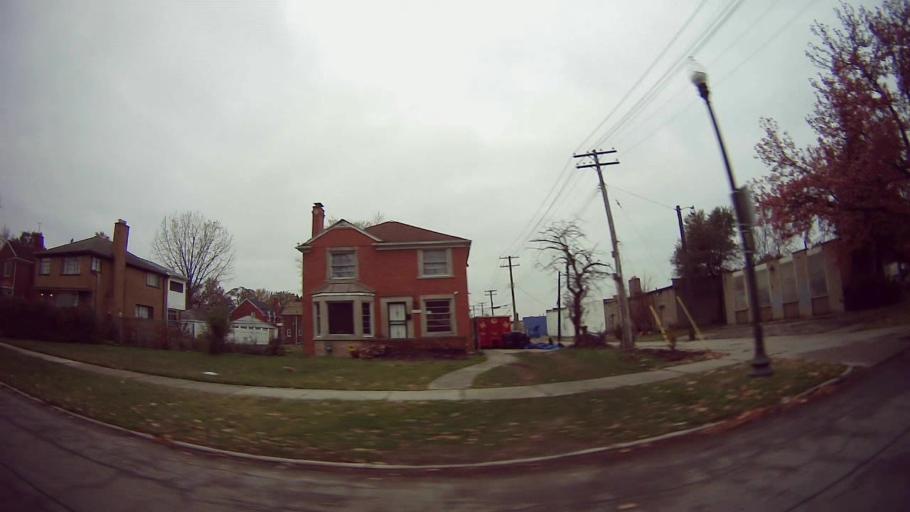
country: US
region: Michigan
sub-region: Oakland County
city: Oak Park
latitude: 42.4307
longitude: -83.1757
